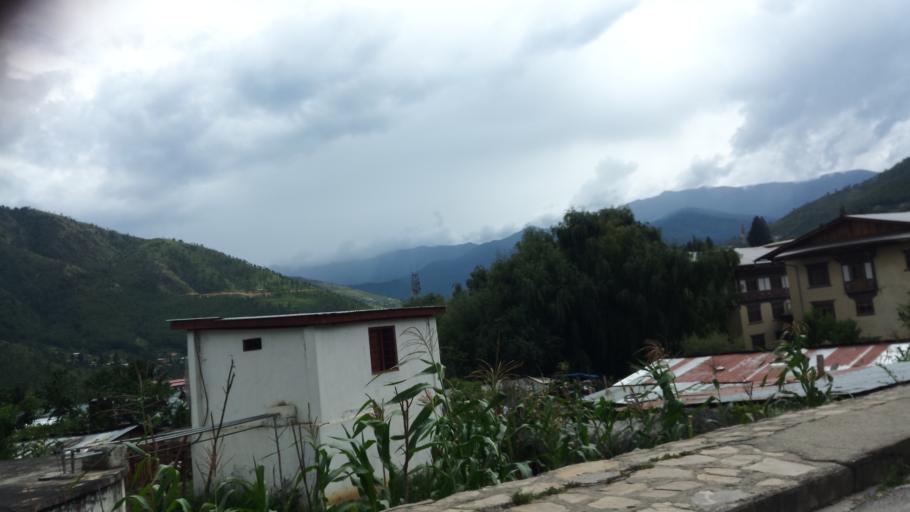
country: BT
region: Thimphu
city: Thimphu
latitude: 27.4721
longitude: 89.6317
